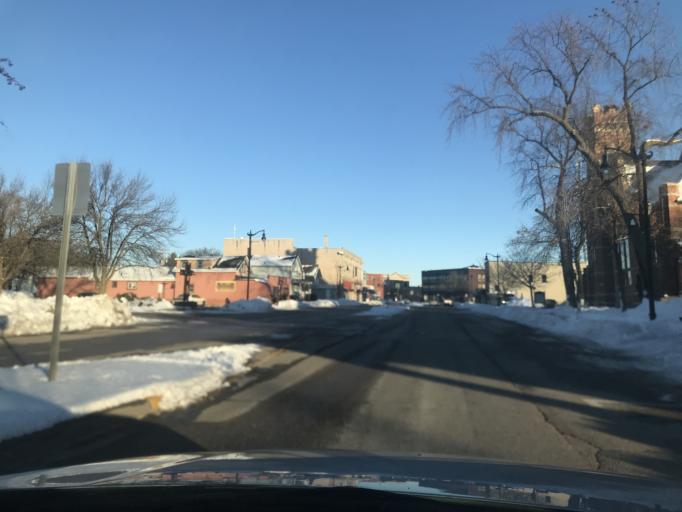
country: US
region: Michigan
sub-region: Menominee County
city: Menominee
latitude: 45.1076
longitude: -87.6088
